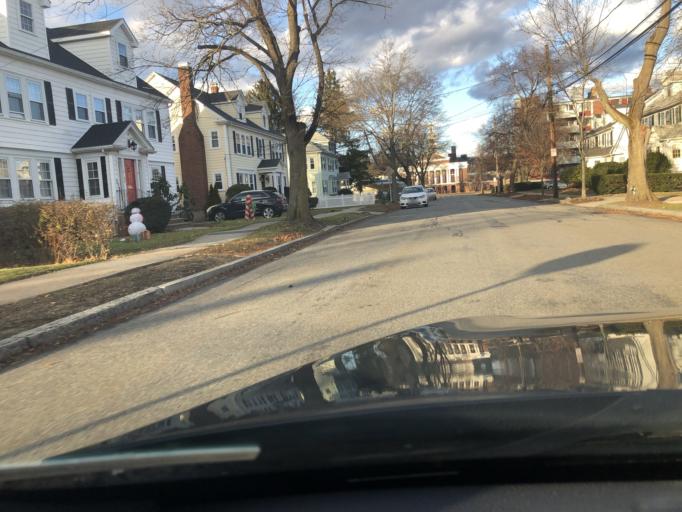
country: US
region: Massachusetts
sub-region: Middlesex County
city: Arlington
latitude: 42.4157
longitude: -71.1621
